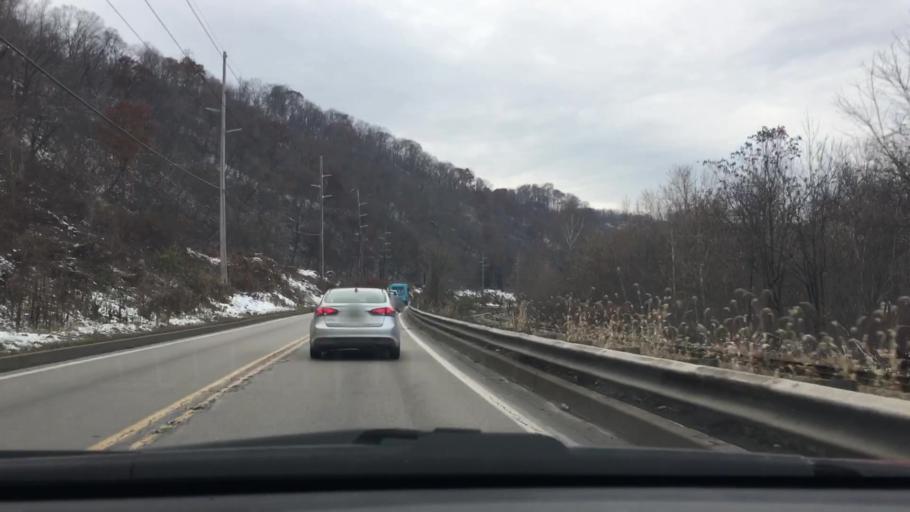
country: US
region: Pennsylvania
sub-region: Allegheny County
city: West Homestead
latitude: 40.3953
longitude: -79.9431
